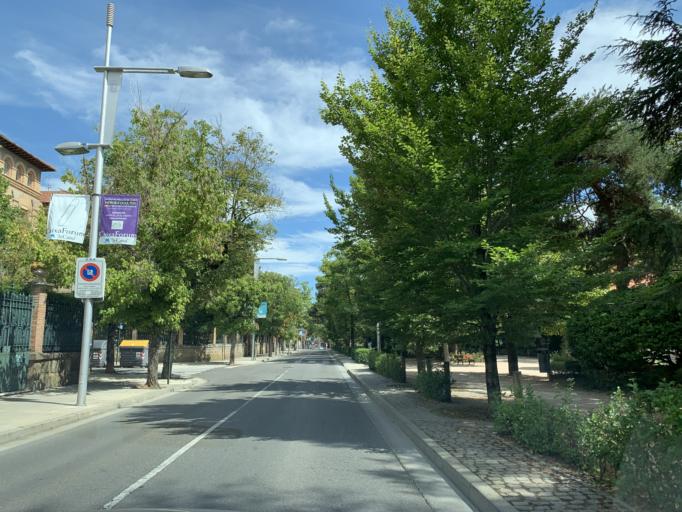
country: ES
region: Aragon
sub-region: Provincia de Huesca
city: Jaca
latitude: 42.5705
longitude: -0.5544
